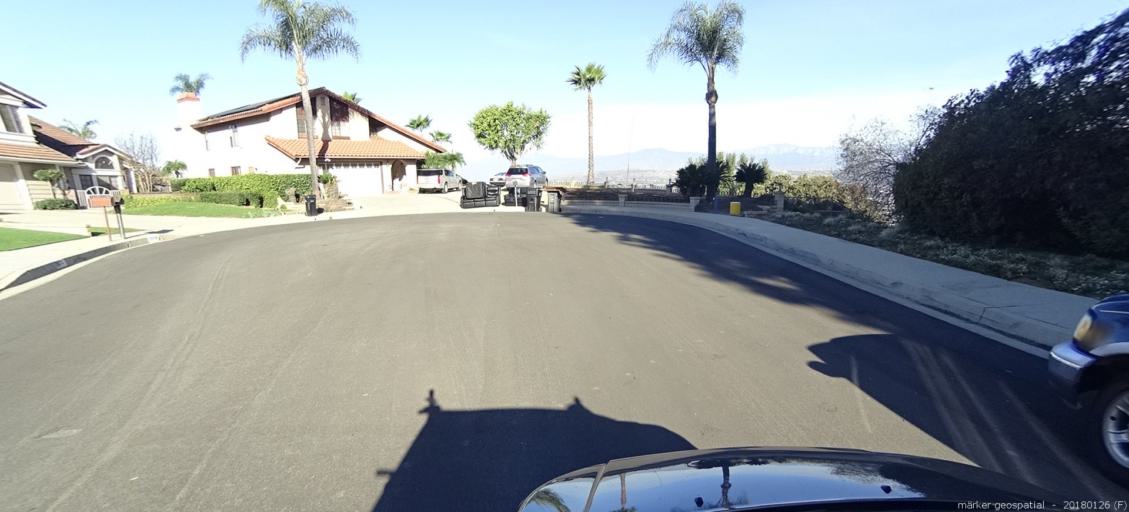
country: US
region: California
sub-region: Los Angeles County
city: Walnut
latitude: 33.9838
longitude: -117.8542
